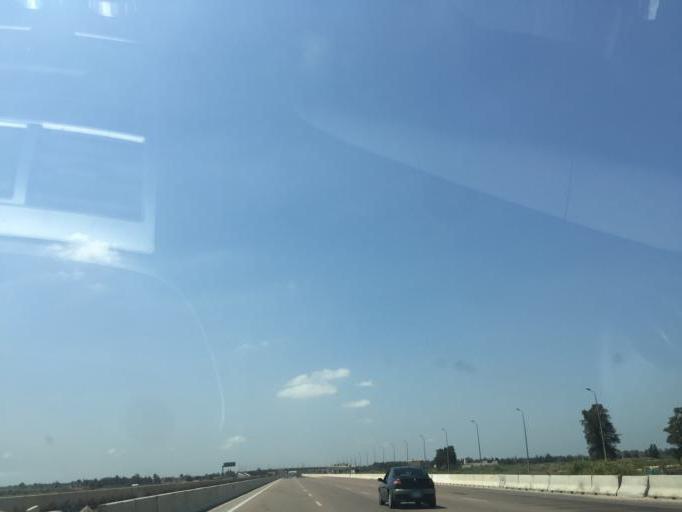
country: EG
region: Al Buhayrah
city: Abu al Matamir
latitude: 30.8797
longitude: 29.8850
